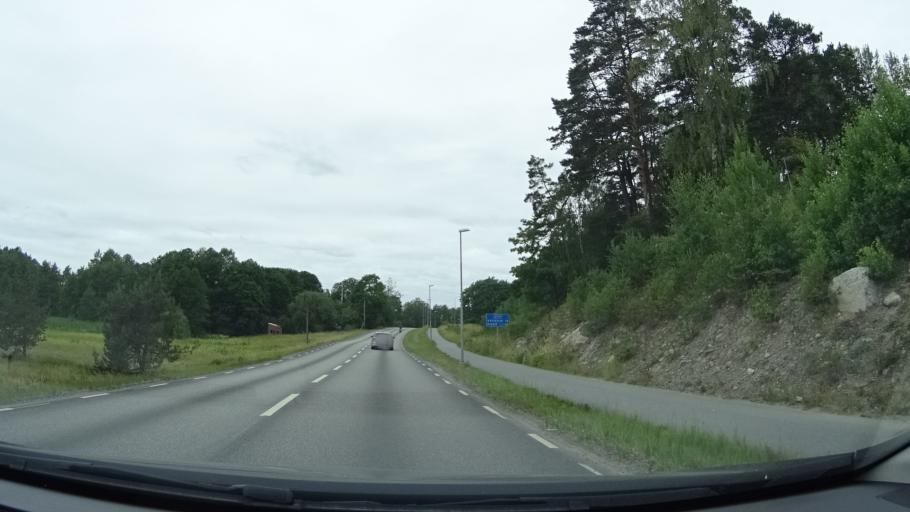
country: SE
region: Stockholm
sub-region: Varmdo Kommun
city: Hemmesta
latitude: 59.3280
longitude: 18.5031
